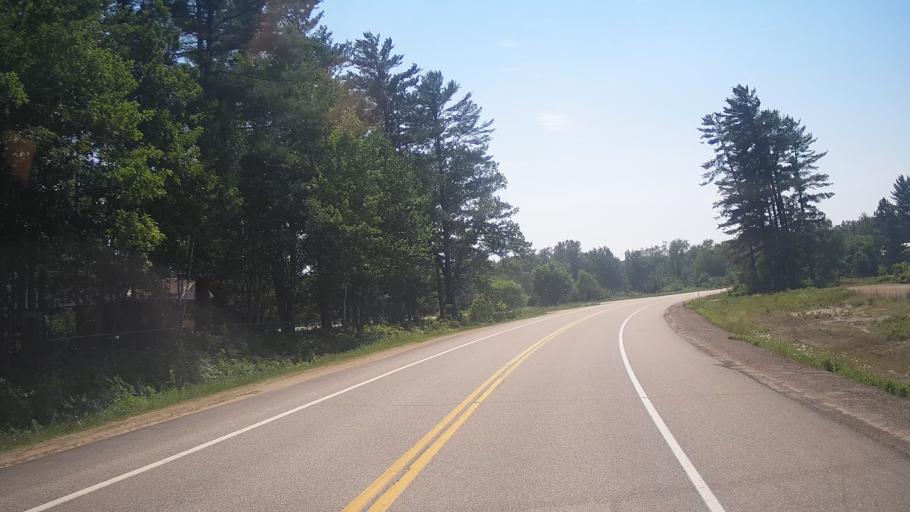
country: CA
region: Quebec
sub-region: Outaouais
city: Fort-Coulonge
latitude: 45.9060
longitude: -76.9237
